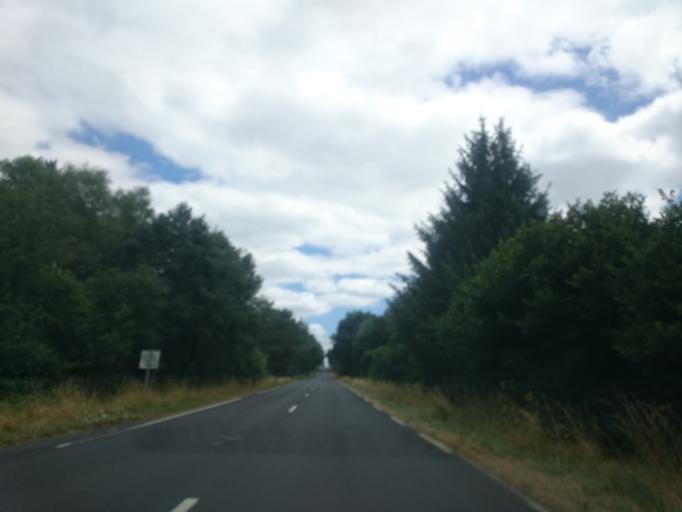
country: FR
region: Auvergne
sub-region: Departement du Cantal
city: Saint-Paul-des-Landes
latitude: 44.9583
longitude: 2.2699
